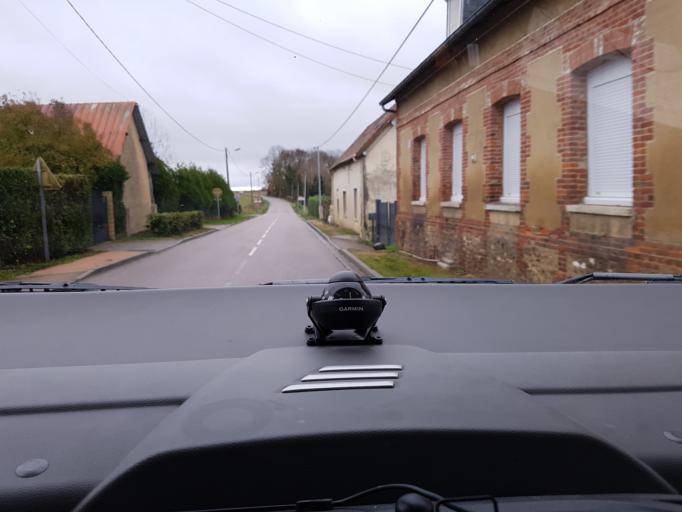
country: FR
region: Haute-Normandie
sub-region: Departement de l'Eure
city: Pont-Saint-Pierre
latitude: 49.3131
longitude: 1.3099
